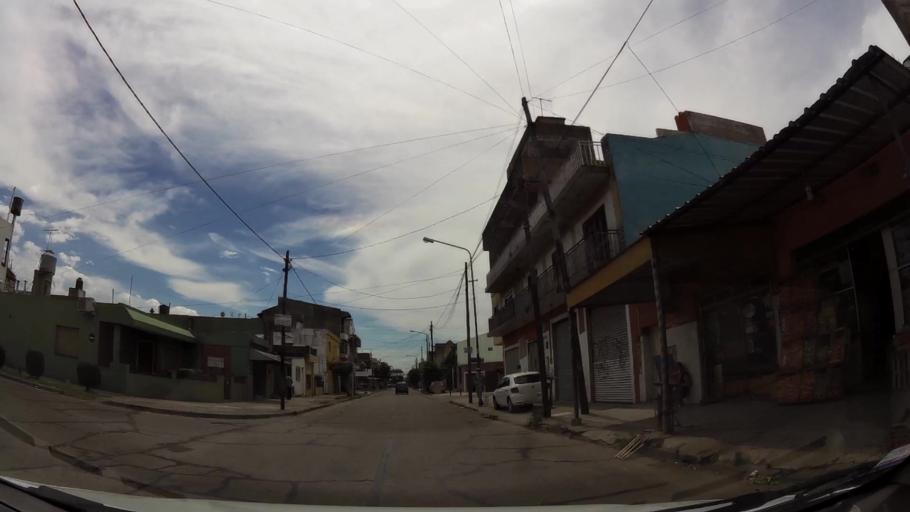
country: AR
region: Buenos Aires
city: San Justo
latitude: -34.6824
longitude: -58.5361
